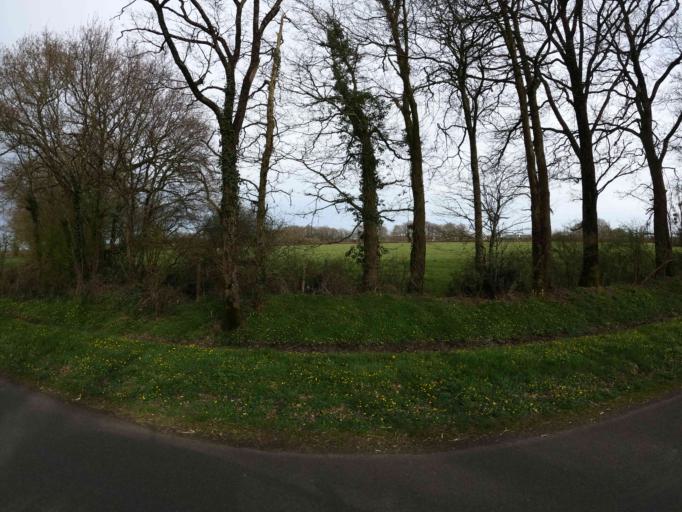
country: FR
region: Pays de la Loire
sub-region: Departement de la Vendee
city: Bouffere
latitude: 46.9611
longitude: -1.3294
